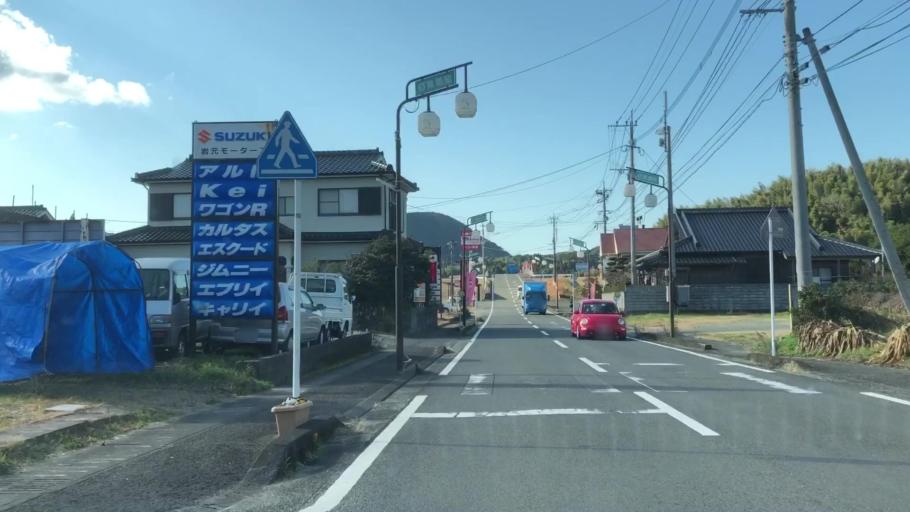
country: JP
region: Kagoshima
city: Satsumasendai
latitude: 31.8642
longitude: 130.3327
